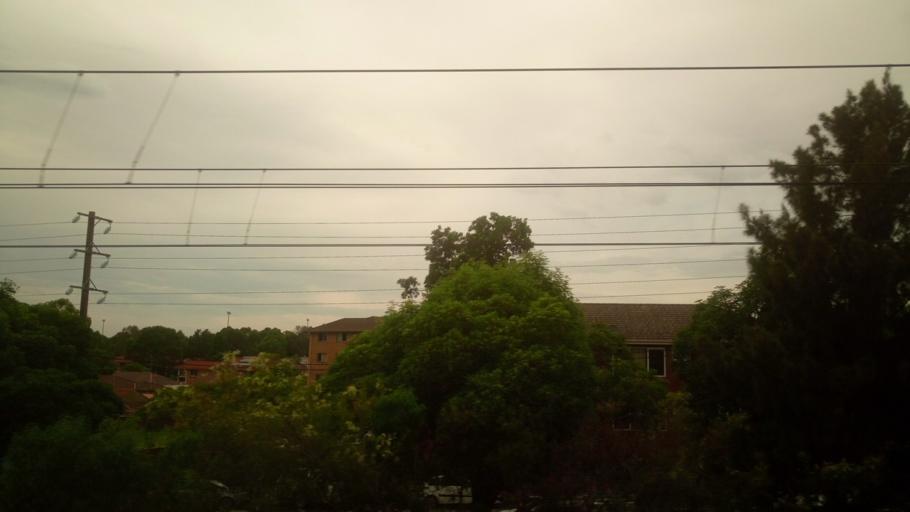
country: AU
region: New South Wales
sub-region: Strathfield
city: Homebush
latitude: -33.8652
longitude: 151.0723
